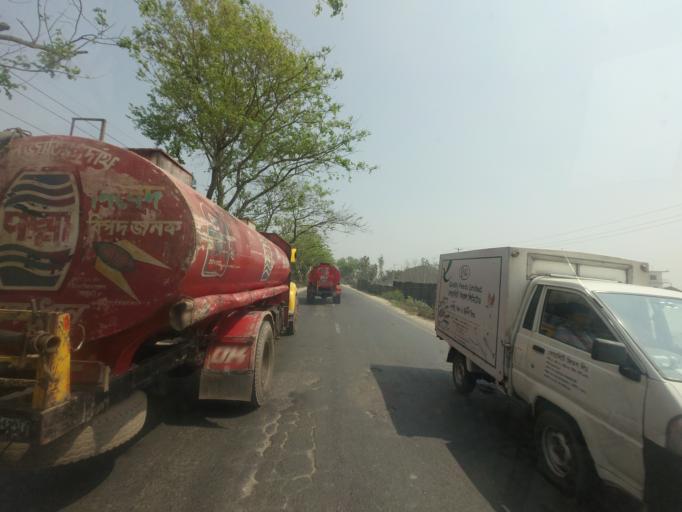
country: BD
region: Dhaka
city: Bhairab Bazar
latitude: 24.0386
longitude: 91.0281
